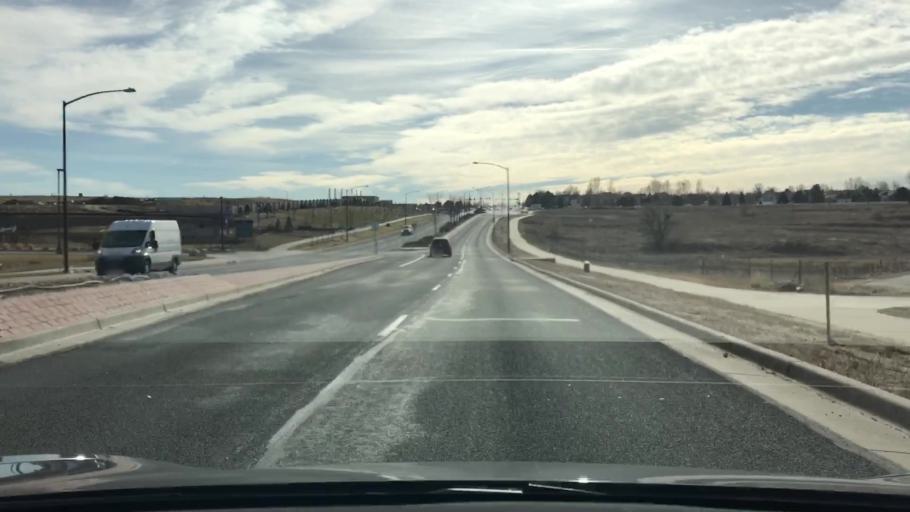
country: US
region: Colorado
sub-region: Adams County
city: Northglenn
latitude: 39.9330
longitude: -104.9971
